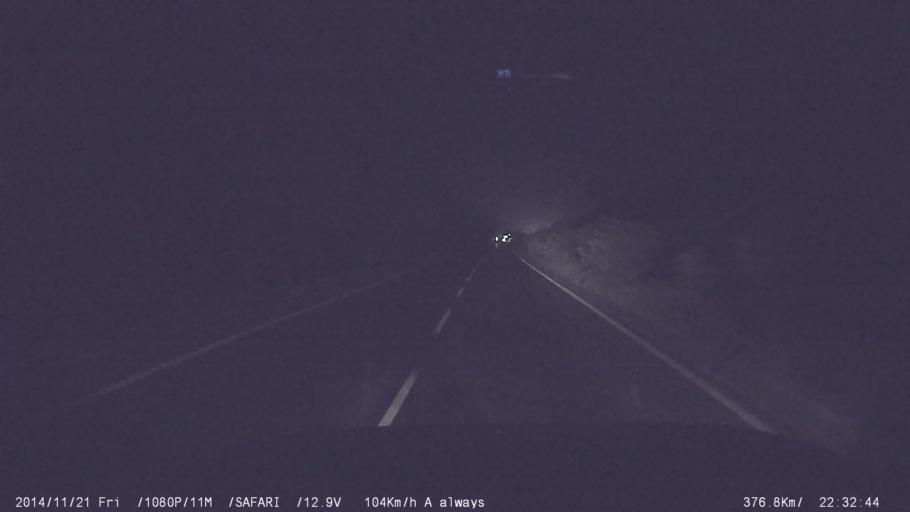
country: IN
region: Tamil Nadu
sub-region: Villupuram
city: Tindivanam
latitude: 12.3127
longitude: 79.7574
